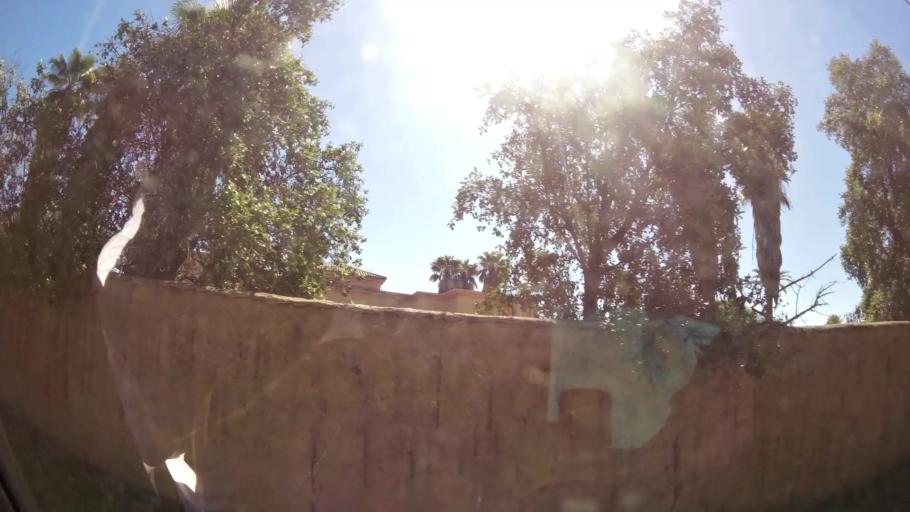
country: MA
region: Marrakech-Tensift-Al Haouz
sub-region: Marrakech
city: Marrakesh
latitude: 31.6638
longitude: -7.9580
